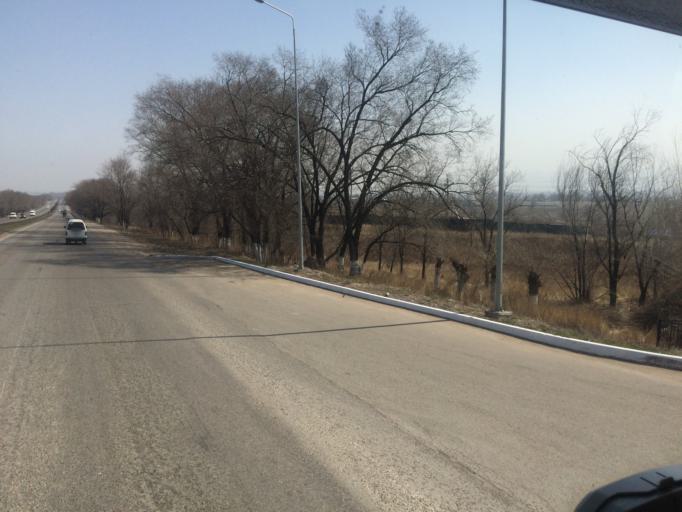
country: KZ
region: Almaty Oblysy
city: Burunday
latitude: 43.2224
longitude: 76.5758
